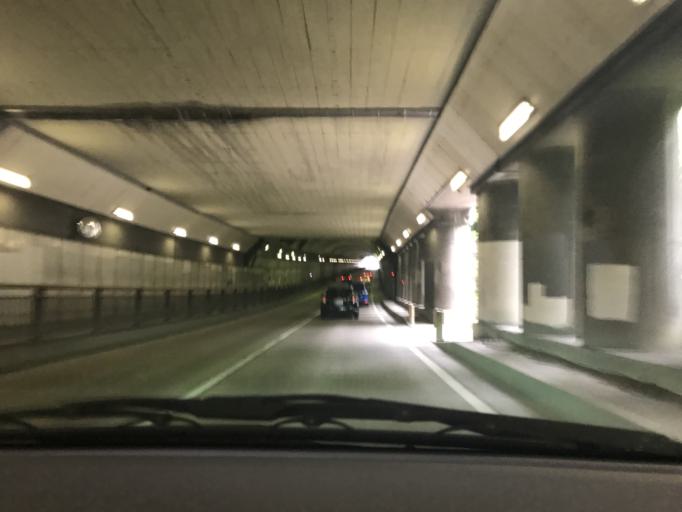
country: JP
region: Kanagawa
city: Fujisawa
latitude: 35.3517
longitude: 139.4449
